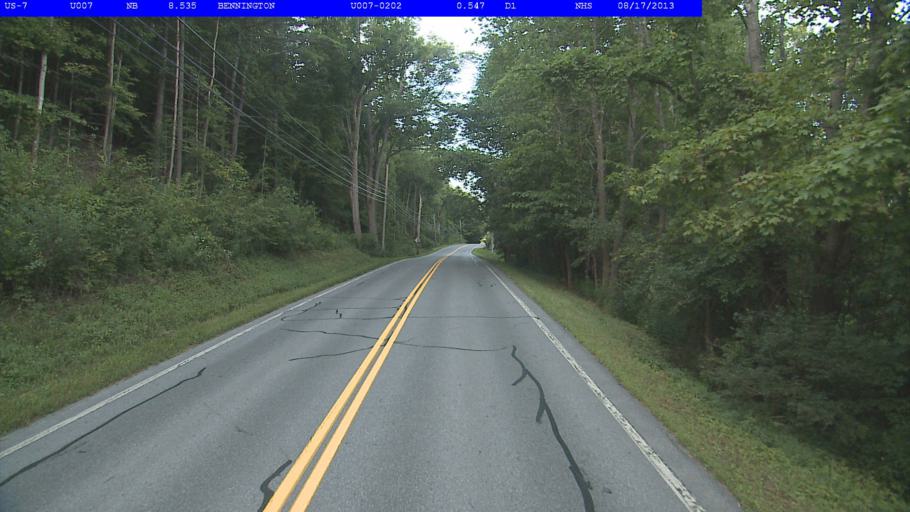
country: US
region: Vermont
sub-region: Bennington County
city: Bennington
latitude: 42.8452
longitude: -73.2018
